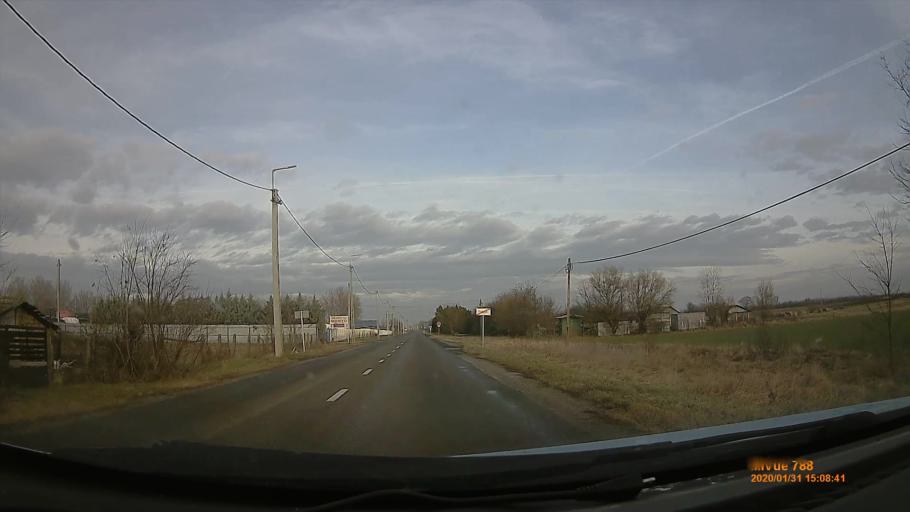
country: HU
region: Hajdu-Bihar
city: Polgar
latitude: 47.8663
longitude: 21.1346
